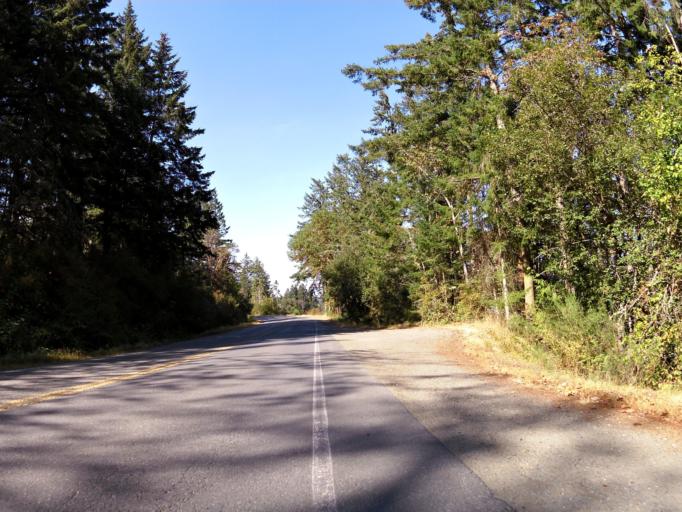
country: CA
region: British Columbia
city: North Saanich
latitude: 48.6267
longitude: -123.5281
